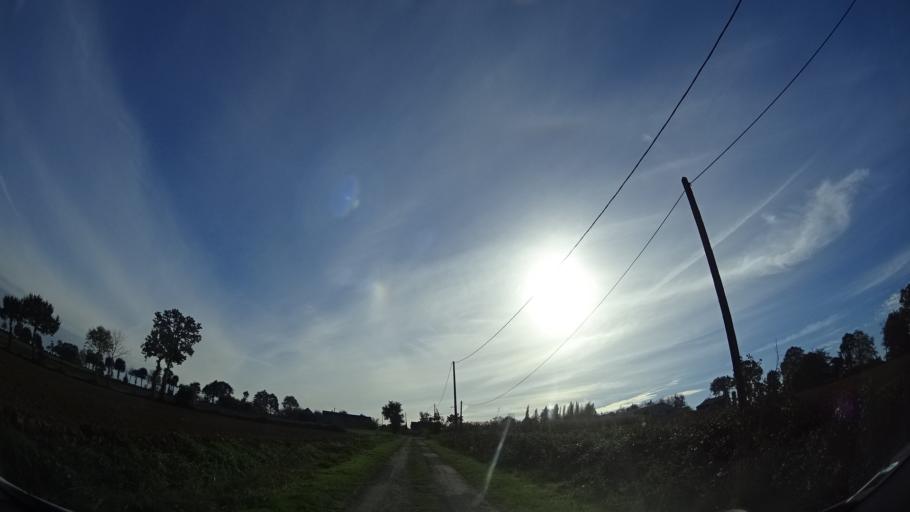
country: FR
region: Brittany
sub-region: Departement d'Ille-et-Vilaine
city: Geveze
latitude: 48.2320
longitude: -1.8263
